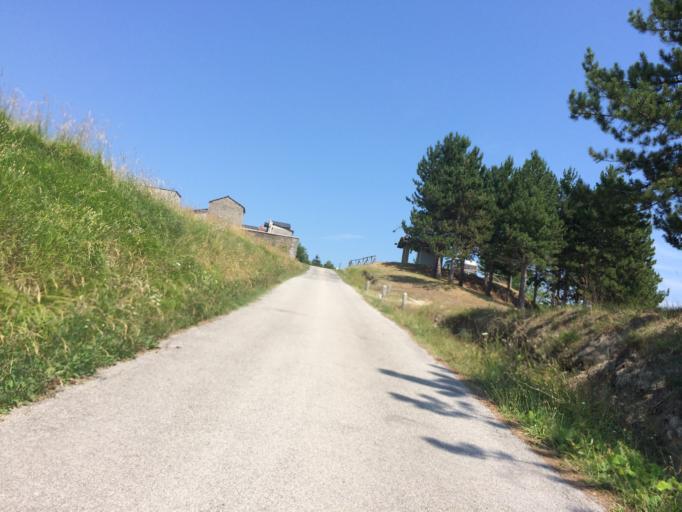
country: IT
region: Piedmont
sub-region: Provincia di Cuneo
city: Serravalle Langhe
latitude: 44.5588
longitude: 8.0522
